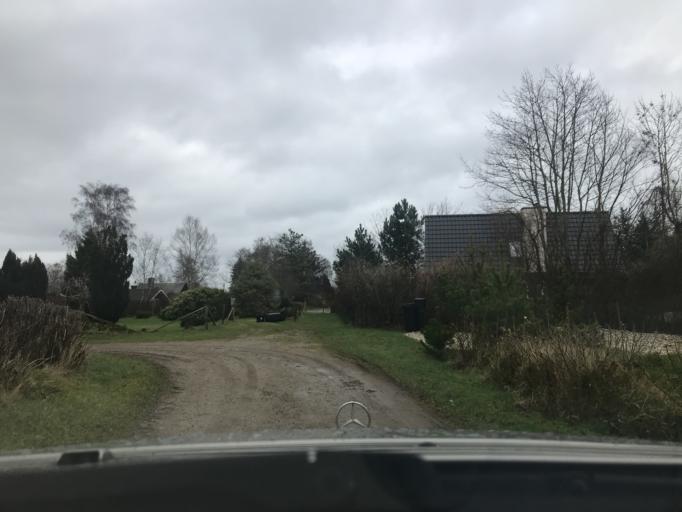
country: DE
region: Schleswig-Holstein
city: Pommerby
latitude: 54.8751
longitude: 10.0278
